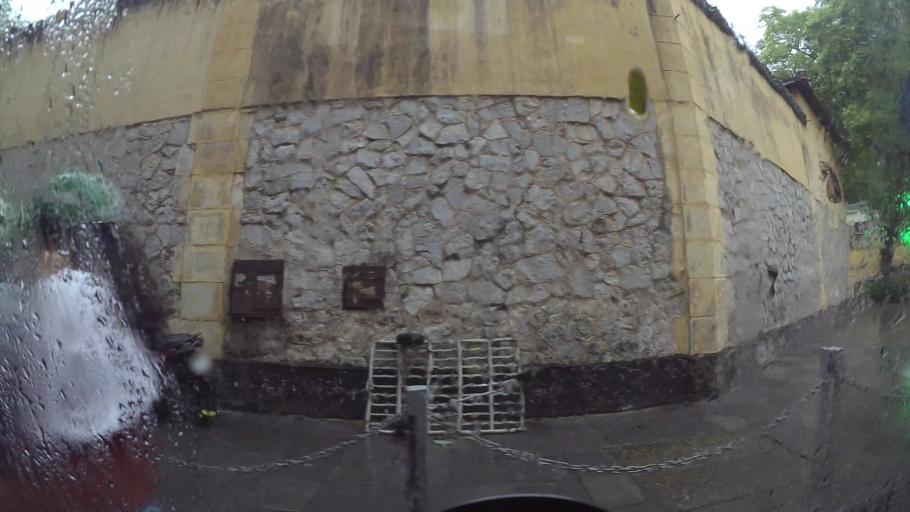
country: VN
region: Ha Noi
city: Hanoi
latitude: 21.0249
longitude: 105.8462
